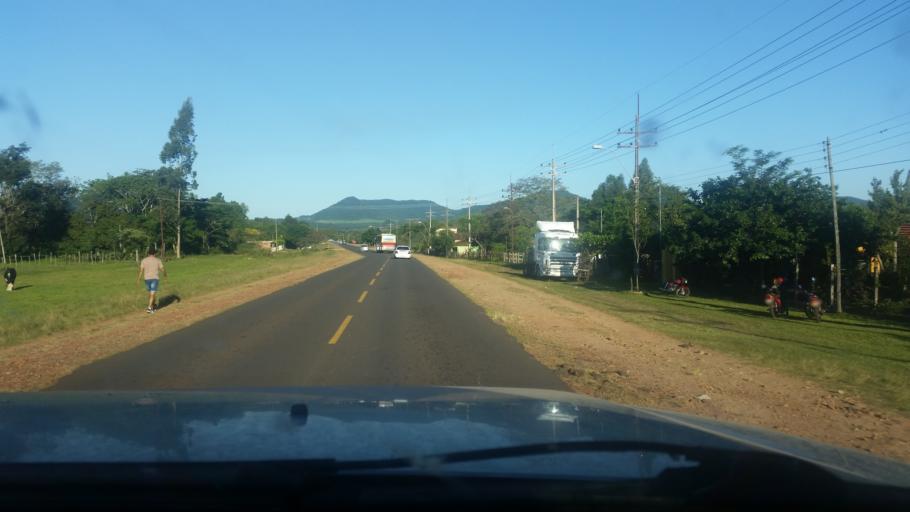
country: PY
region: Guaira
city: Mbocayaty
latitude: -25.7179
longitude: -56.3351
